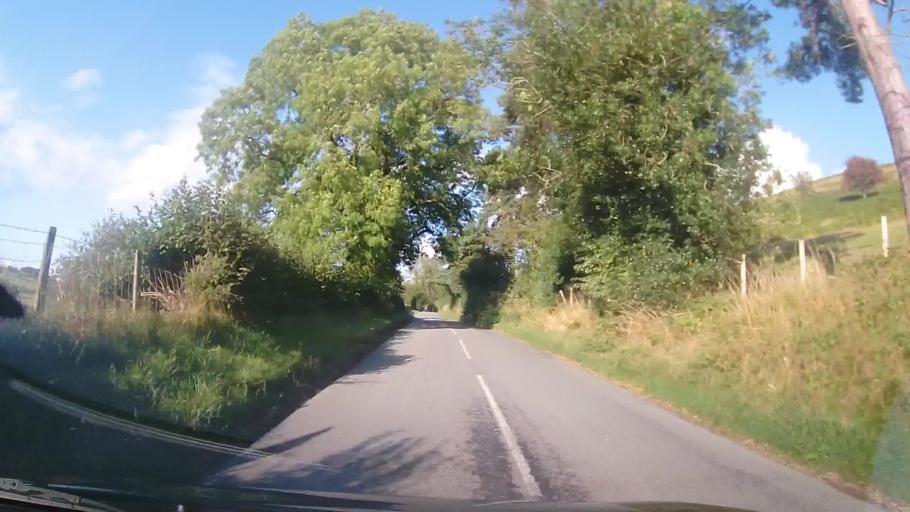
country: GB
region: England
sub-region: Shropshire
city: Pontesbury
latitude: 52.5742
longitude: -2.8871
